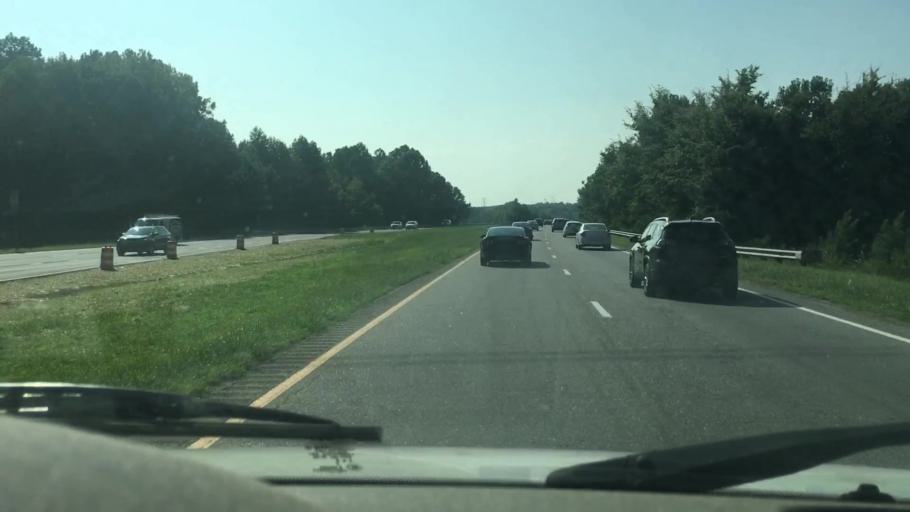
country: US
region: North Carolina
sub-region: Gaston County
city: Mount Holly
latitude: 35.3532
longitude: -80.9758
